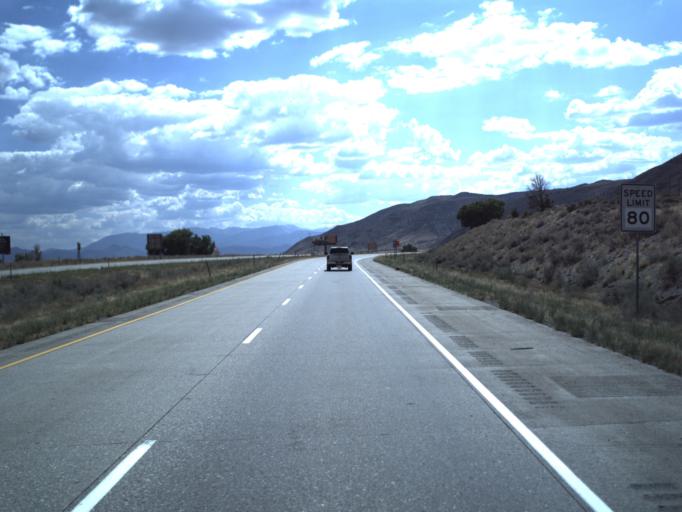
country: US
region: Utah
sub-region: Sevier County
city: Richfield
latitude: 38.7357
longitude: -112.1164
